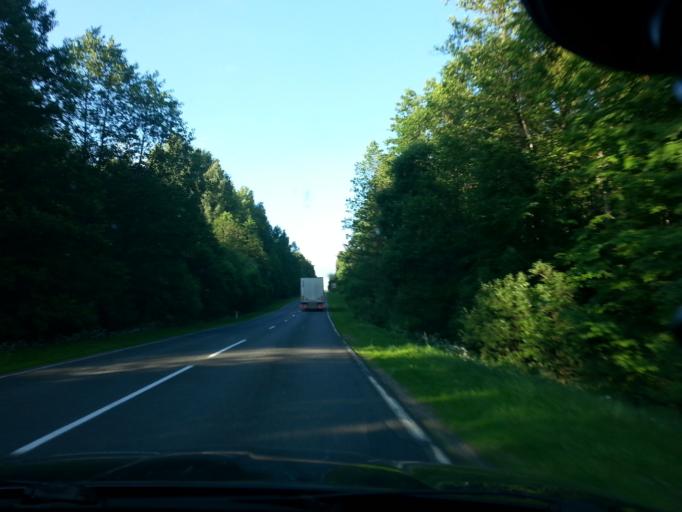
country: BY
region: Minsk
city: Svir
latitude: 54.8720
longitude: 26.3515
